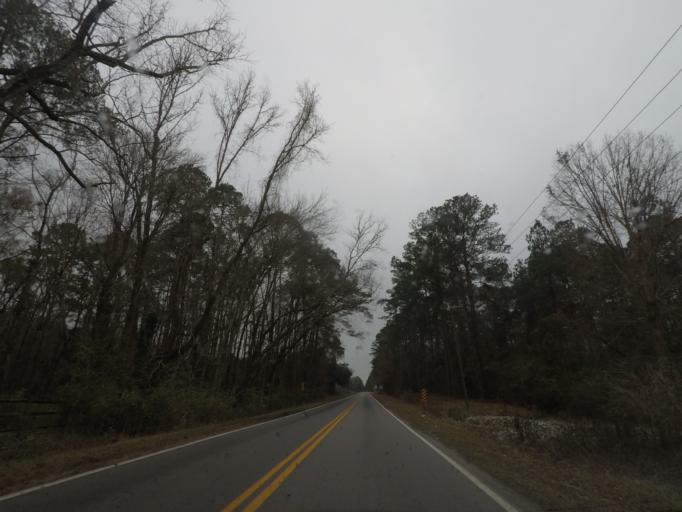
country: US
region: South Carolina
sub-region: Charleston County
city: Ravenel
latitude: 32.7536
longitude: -80.3465
